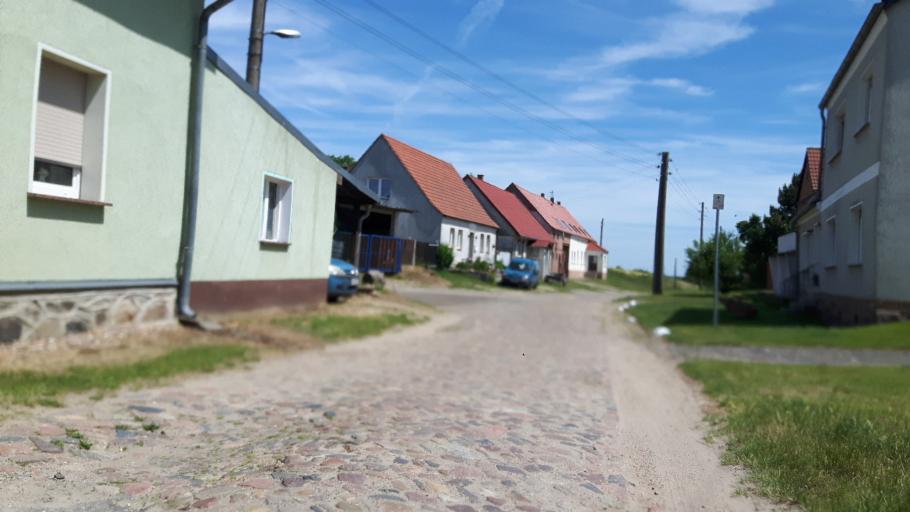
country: DE
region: Saxony-Anhalt
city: Kropstadt
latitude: 52.0068
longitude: 12.7235
